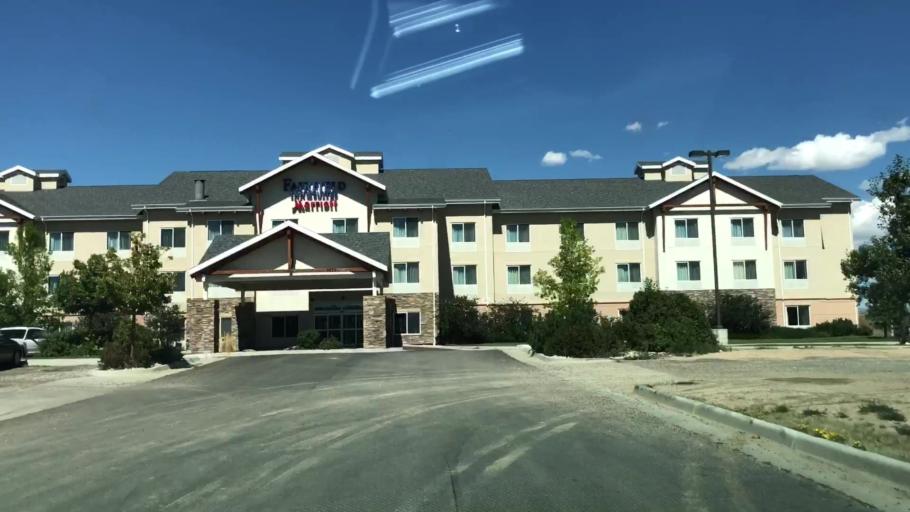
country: US
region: Wyoming
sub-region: Albany County
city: Laramie
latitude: 41.3248
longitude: -105.6187
